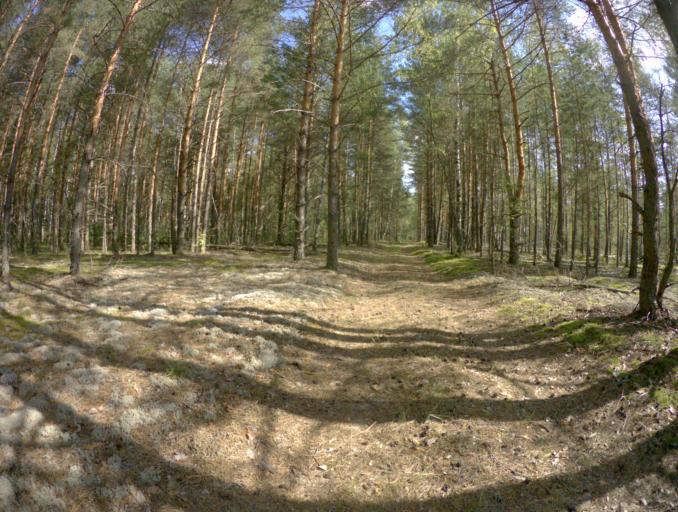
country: RU
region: Vladimir
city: Pokrov
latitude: 55.8450
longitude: 39.2126
